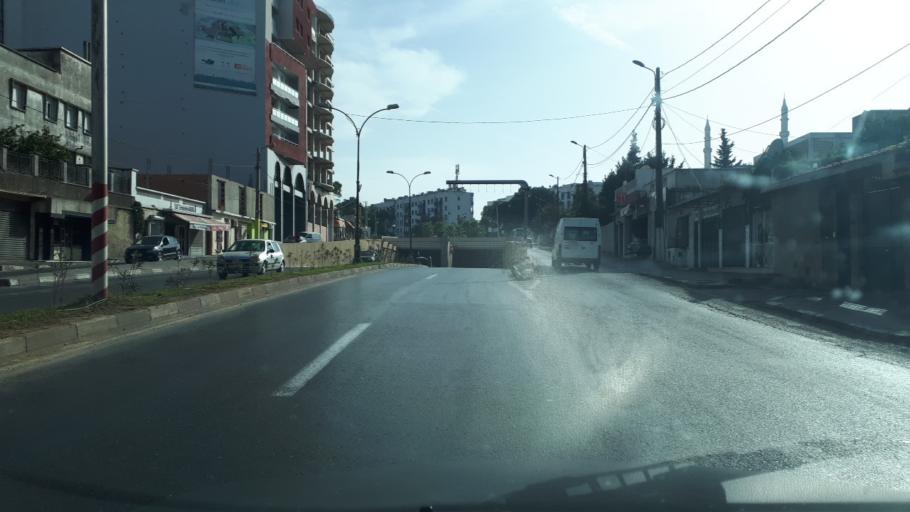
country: DZ
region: Alger
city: Algiers
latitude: 36.7698
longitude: 3.0118
